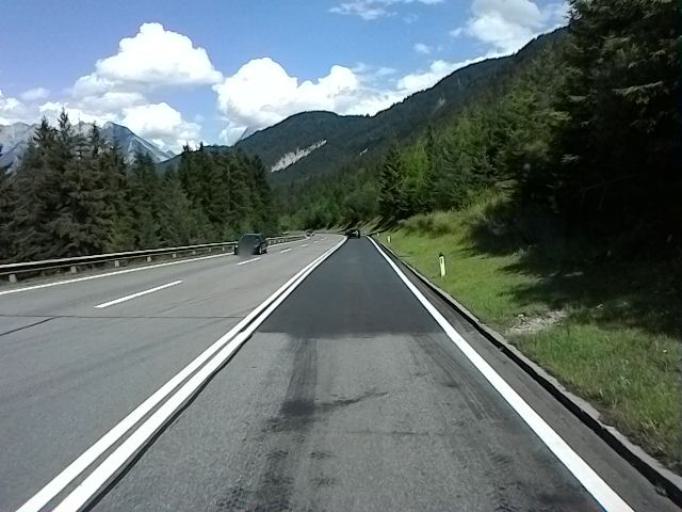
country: AT
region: Tyrol
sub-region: Politischer Bezirk Innsbruck Land
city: Seefeld in Tirol
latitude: 47.3461
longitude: 11.2082
